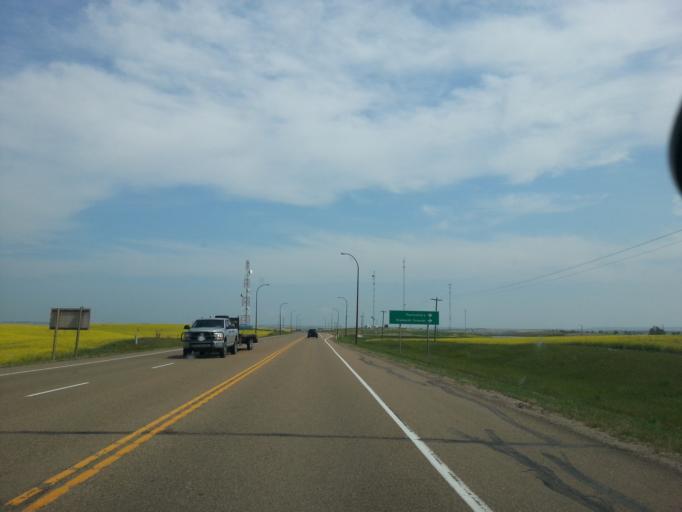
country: CA
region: Alberta
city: Three Hills
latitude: 51.4260
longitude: -112.7142
